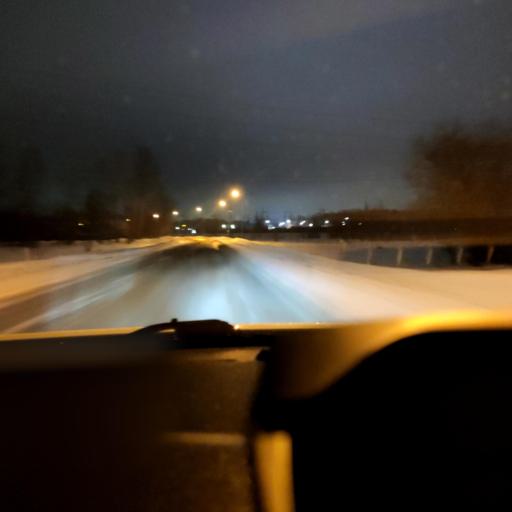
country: RU
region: Tatarstan
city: Vysokaya Gora
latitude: 55.8870
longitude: 49.2402
